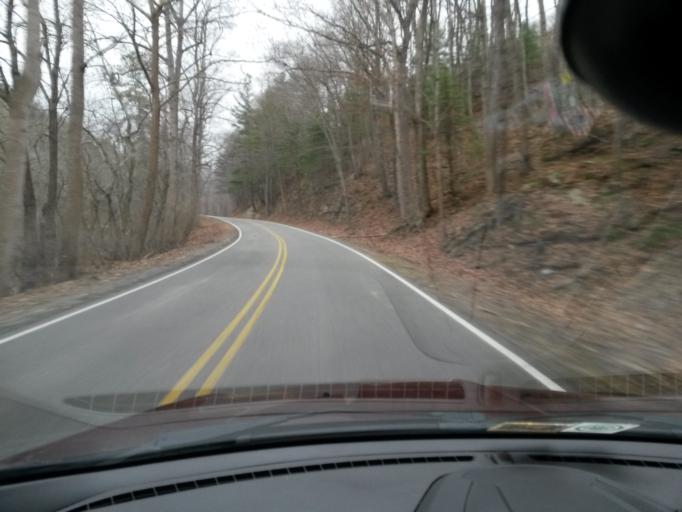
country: US
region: Virginia
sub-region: Rockbridge County
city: East Lexington
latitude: 37.9672
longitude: -79.4990
